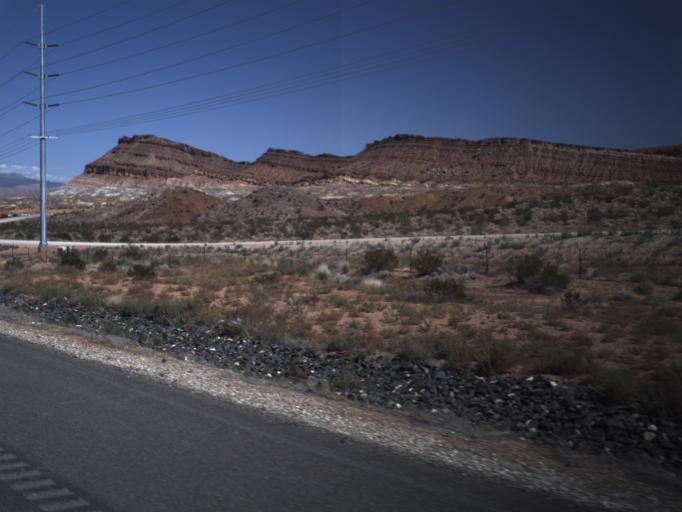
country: US
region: Utah
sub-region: Washington County
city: Washington
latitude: 37.0548
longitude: -113.4857
